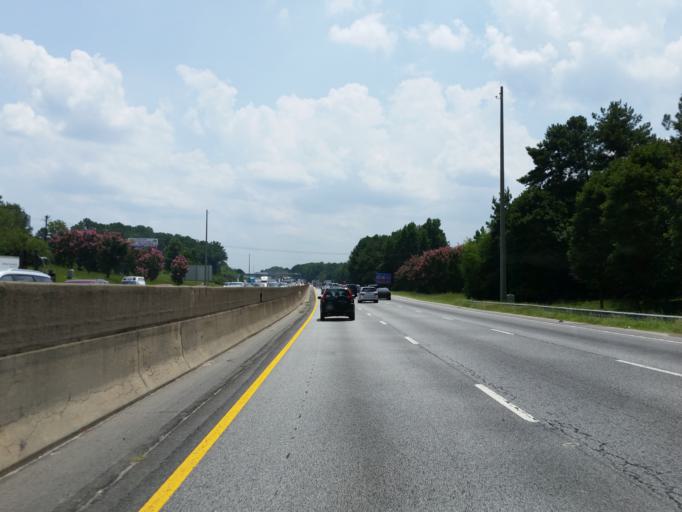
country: US
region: Georgia
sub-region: Clayton County
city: Forest Park
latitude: 33.6274
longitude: -84.4004
